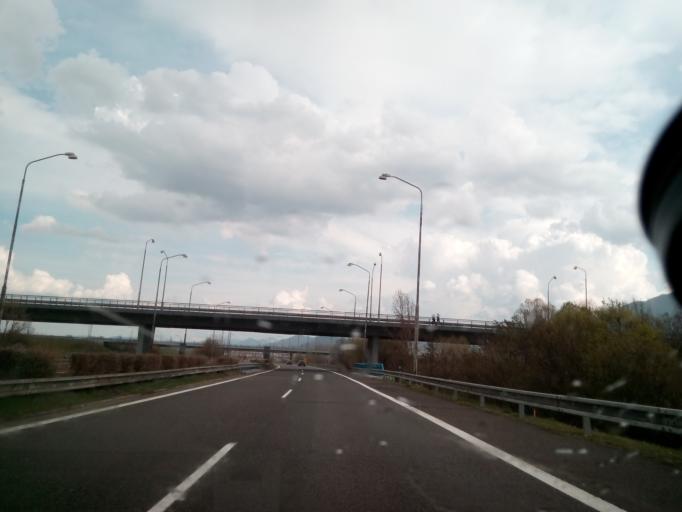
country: SK
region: Zilinsky
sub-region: Okres Liptovsky Mikulas
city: Liptovsky Mikulas
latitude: 49.0756
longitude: 19.5957
